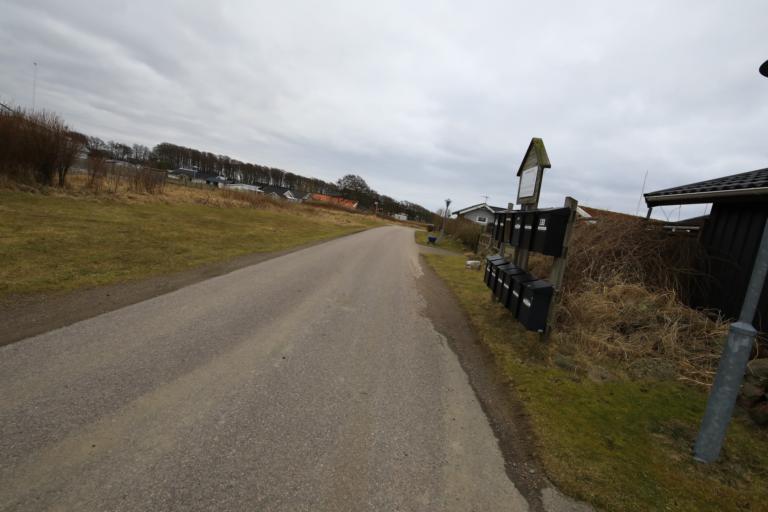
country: SE
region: Halland
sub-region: Varbergs Kommun
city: Traslovslage
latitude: 57.0693
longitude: 12.2782
